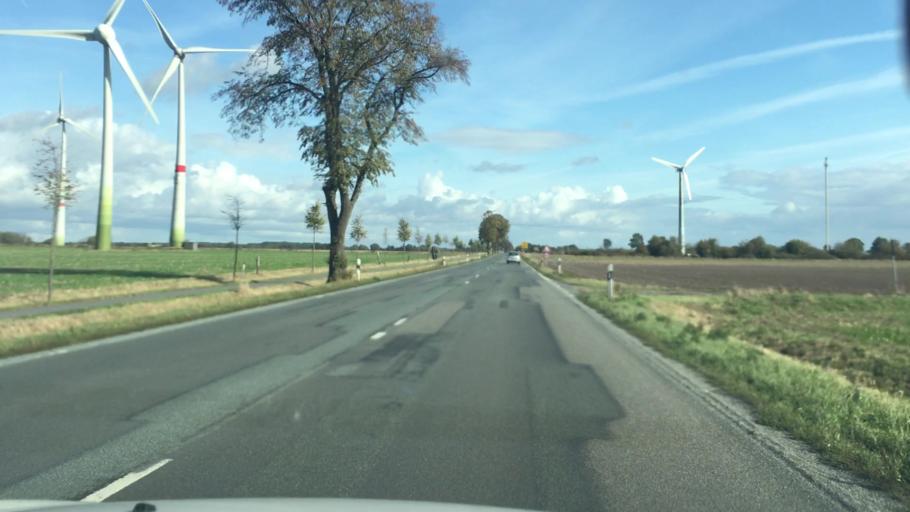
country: DE
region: Lower Saxony
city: Siedenburg
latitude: 52.6726
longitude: 8.9407
